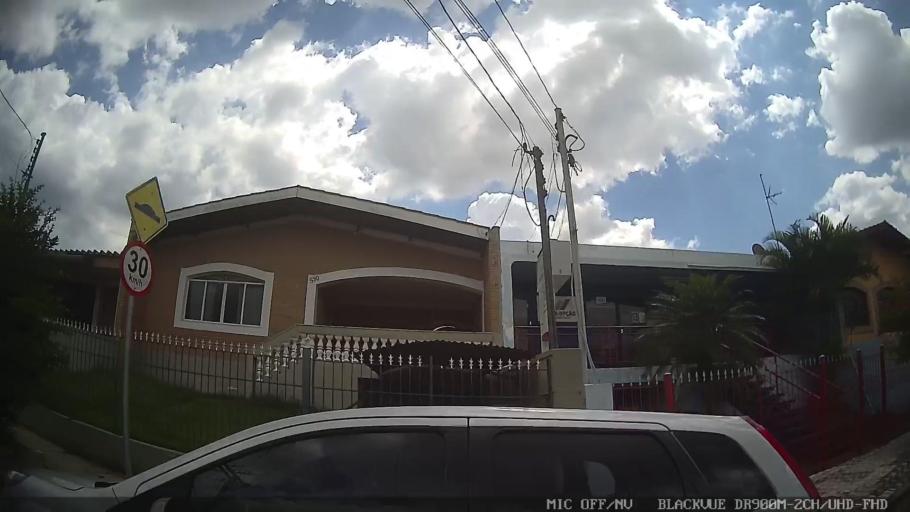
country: BR
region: Sao Paulo
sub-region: Atibaia
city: Atibaia
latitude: -23.1210
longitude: -46.5631
